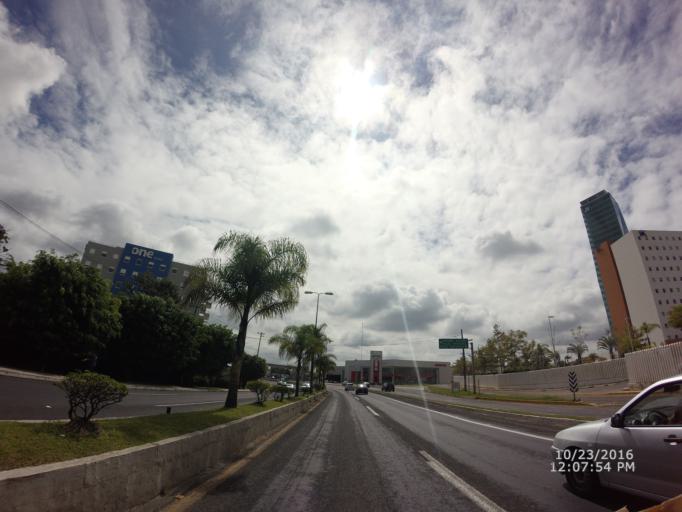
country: MX
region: Veracruz
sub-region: Xalapa
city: Colonia Santa Barbara
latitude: 19.5163
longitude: -96.8804
